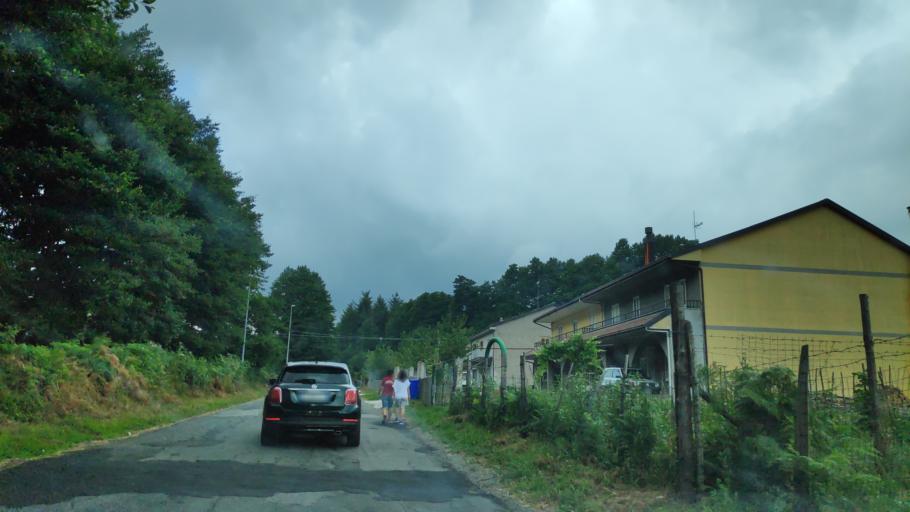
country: IT
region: Calabria
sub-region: Provincia di Vibo-Valentia
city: Mongiana
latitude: 38.5282
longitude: 16.3208
